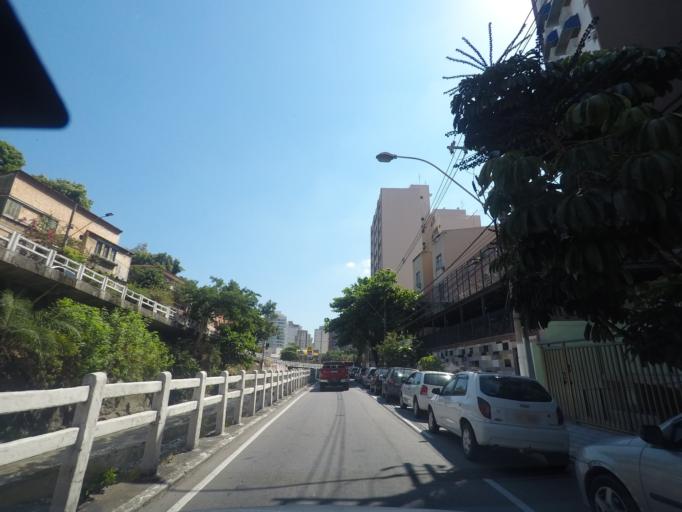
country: BR
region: Rio de Janeiro
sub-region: Niteroi
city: Niteroi
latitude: -22.9107
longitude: -43.1057
